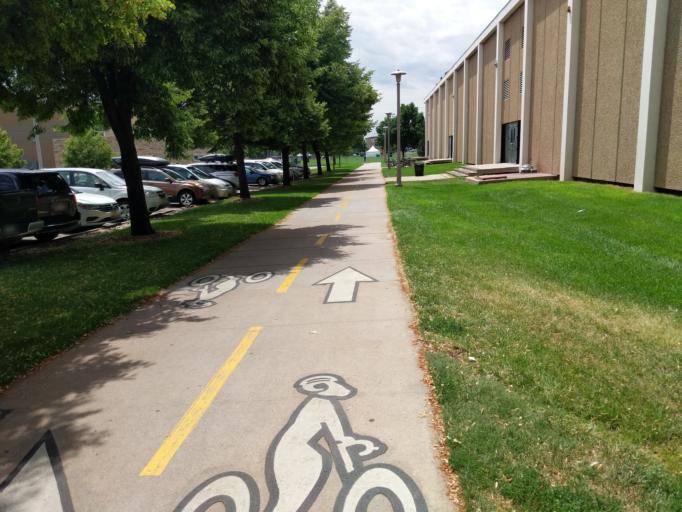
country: US
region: Colorado
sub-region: Larimer County
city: Fort Collins
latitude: 40.5761
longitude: -105.0911
